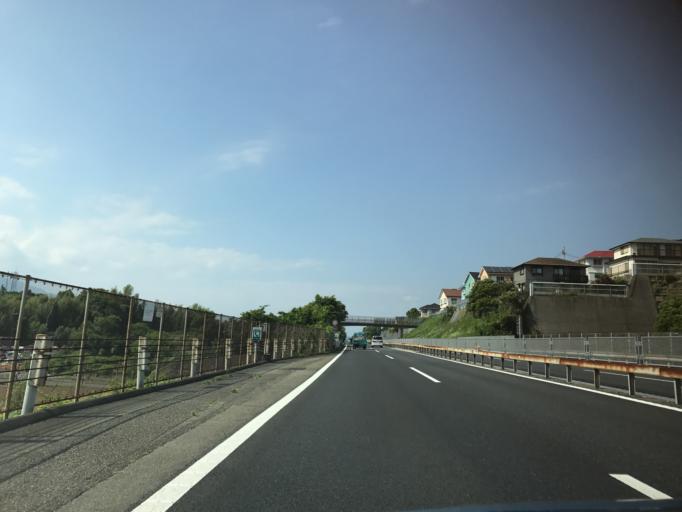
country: JP
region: Kanagawa
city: Oiso
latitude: 35.3405
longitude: 139.2962
